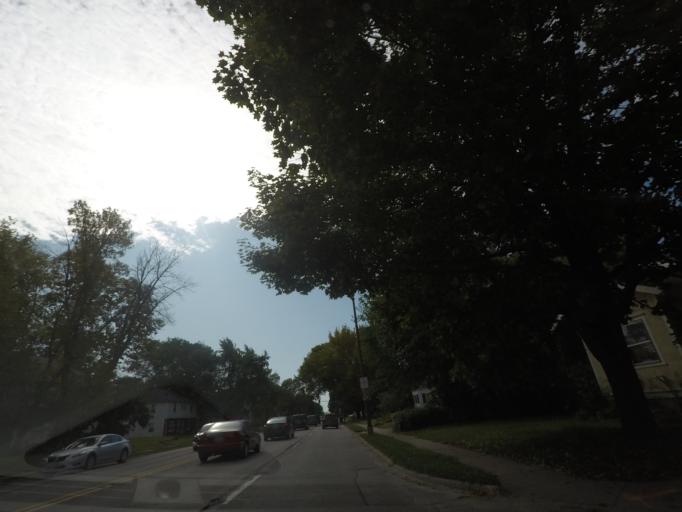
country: US
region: Iowa
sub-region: Story County
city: Ames
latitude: 42.0313
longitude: -93.6204
